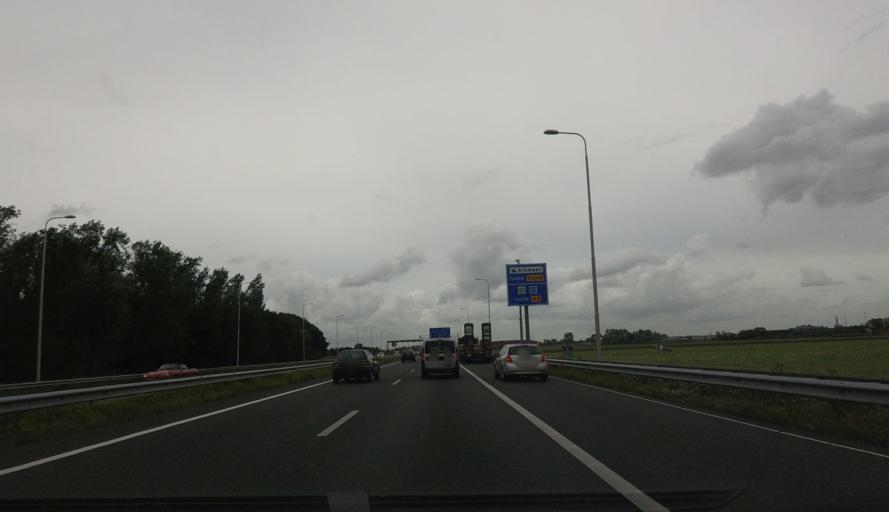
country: NL
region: North Holland
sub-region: Gemeente Alkmaar
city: Alkmaar
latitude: 52.5989
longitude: 4.7280
